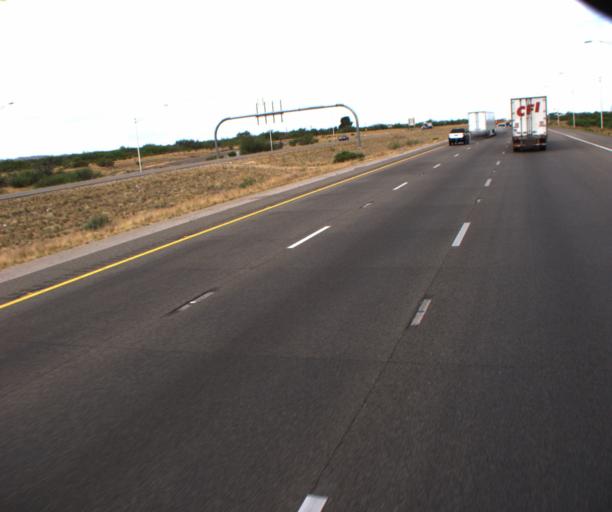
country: US
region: Arizona
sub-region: Cochise County
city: Whetstone
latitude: 31.9636
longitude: -110.3580
